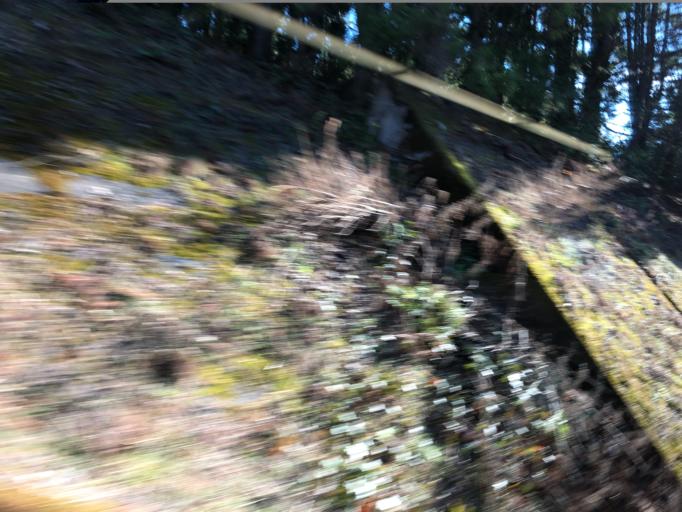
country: JP
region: Kochi
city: Nakamura
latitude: 33.1165
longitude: 133.1130
